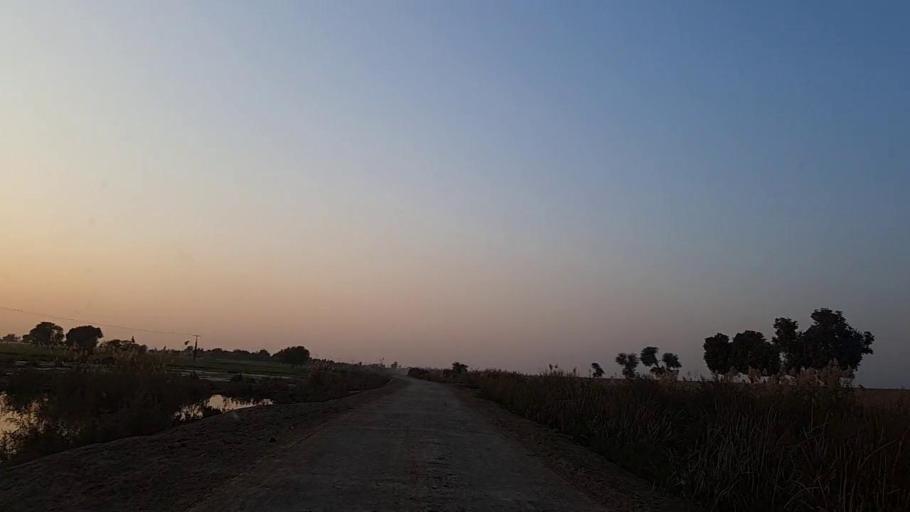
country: PK
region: Sindh
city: Bhit Shah
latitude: 25.9213
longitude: 68.4927
